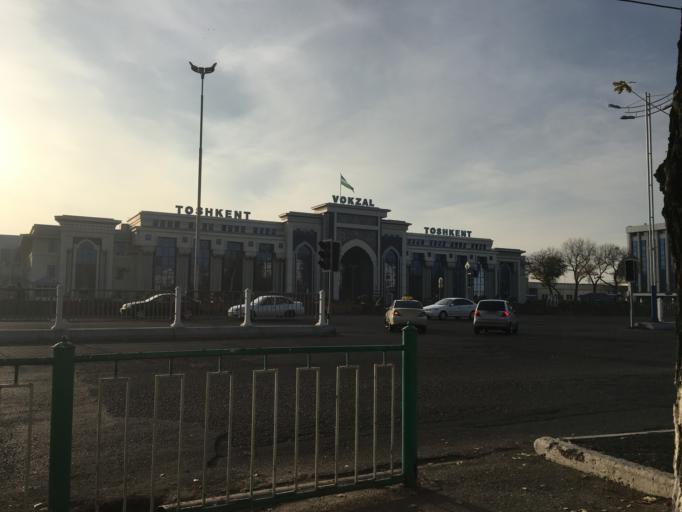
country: UZ
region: Toshkent Shahri
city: Tashkent
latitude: 41.2926
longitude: 69.2862
